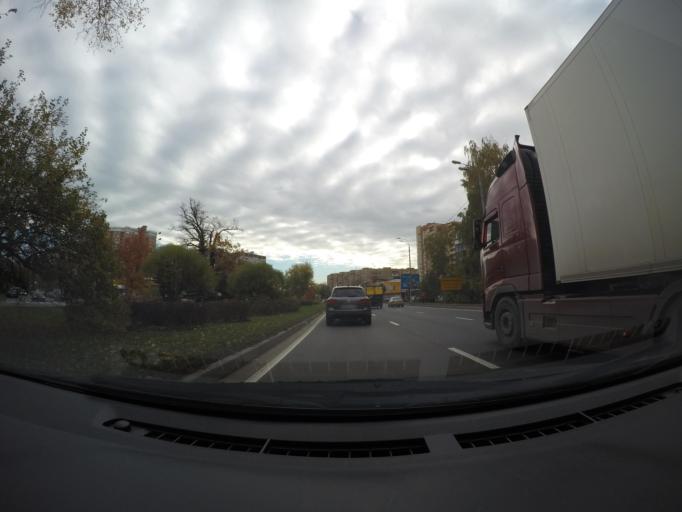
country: RU
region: Moskovskaya
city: Mytishchi
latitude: 55.9267
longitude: 37.7532
